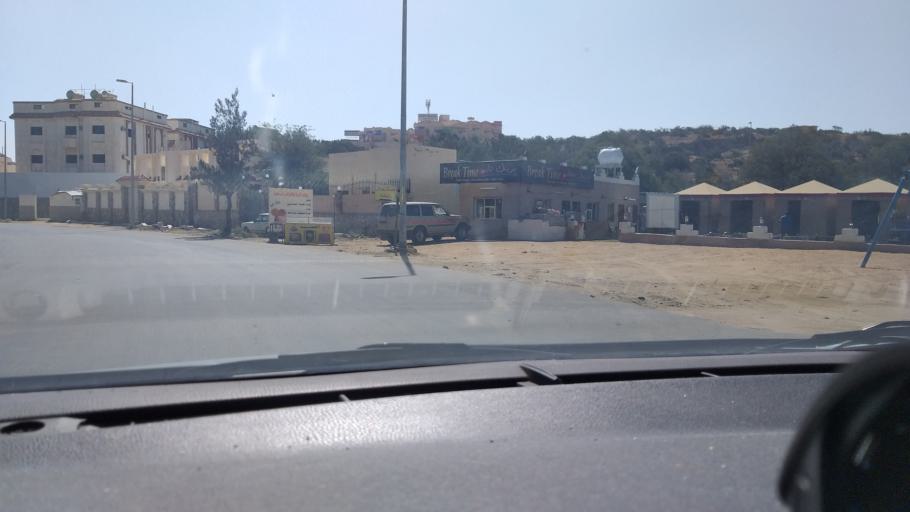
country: SA
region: Makkah
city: Ash Shafa
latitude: 21.0630
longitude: 40.3187
